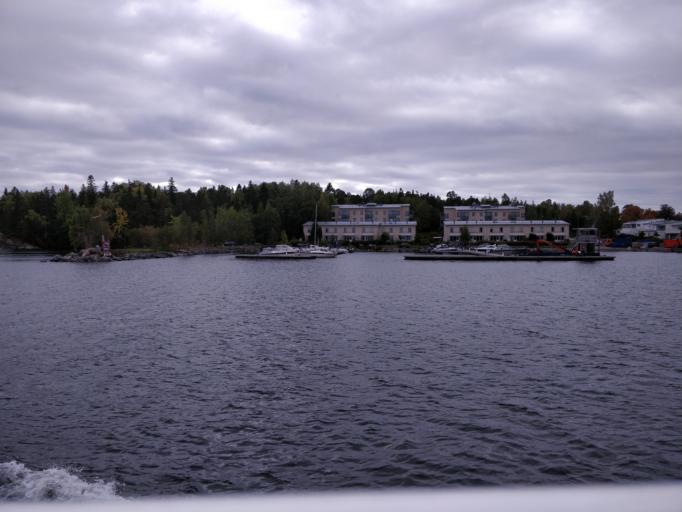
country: FI
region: Uusimaa
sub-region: Helsinki
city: Vantaa
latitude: 60.1736
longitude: 25.0854
